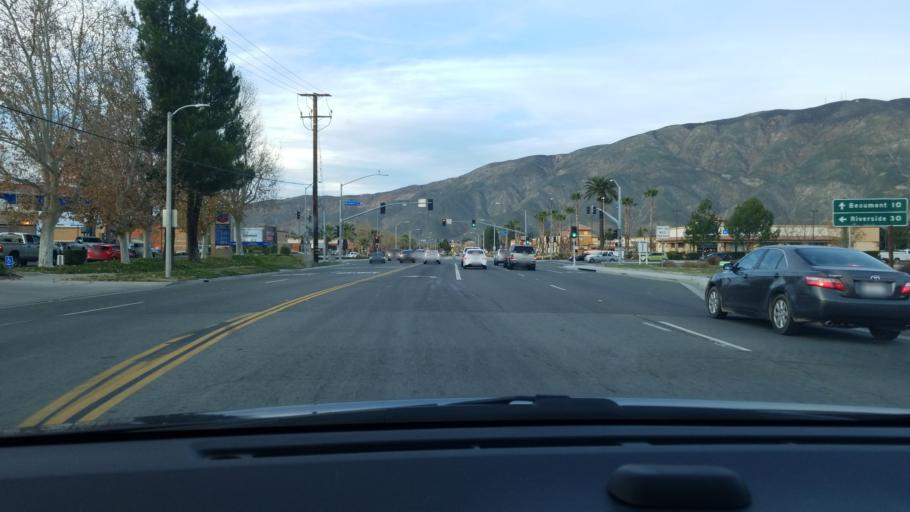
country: US
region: California
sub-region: Riverside County
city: San Jacinto
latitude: 33.8009
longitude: -116.9721
